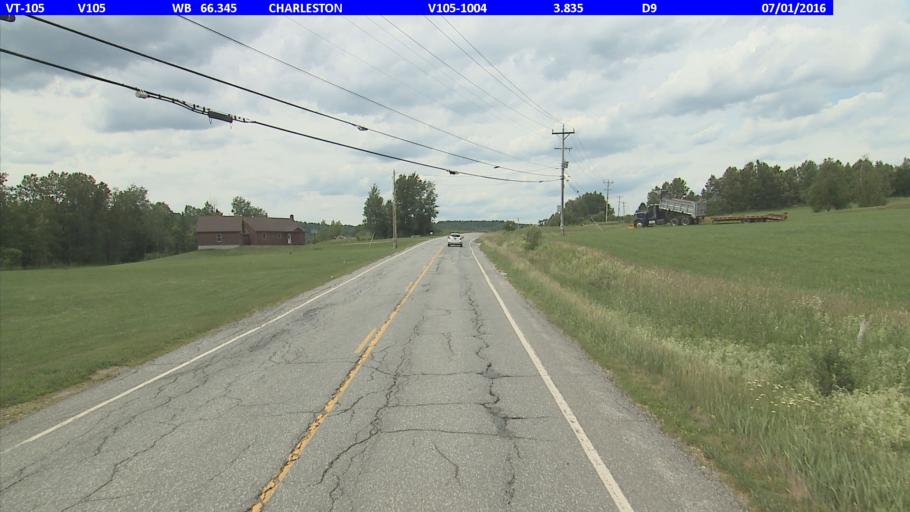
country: US
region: Vermont
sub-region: Orleans County
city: Newport
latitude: 44.8638
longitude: -72.0406
